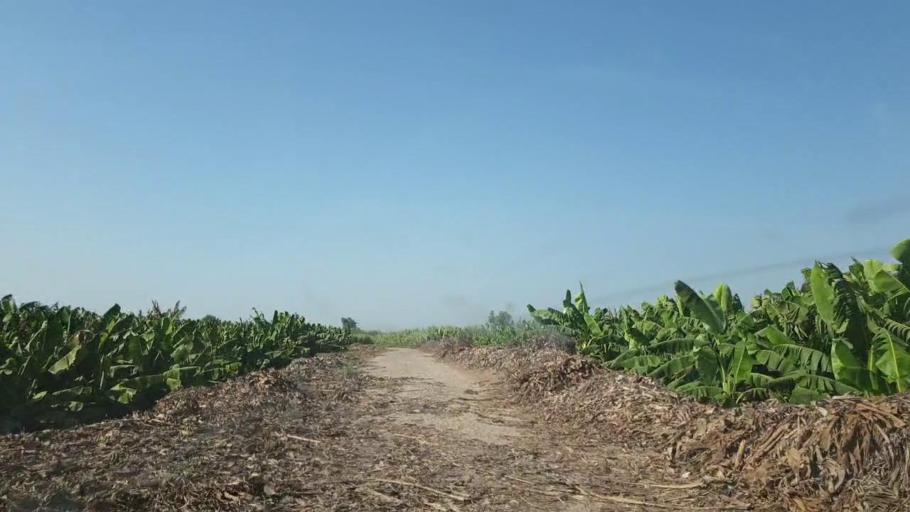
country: PK
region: Sindh
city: Tando Jam
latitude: 25.3403
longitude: 68.5865
